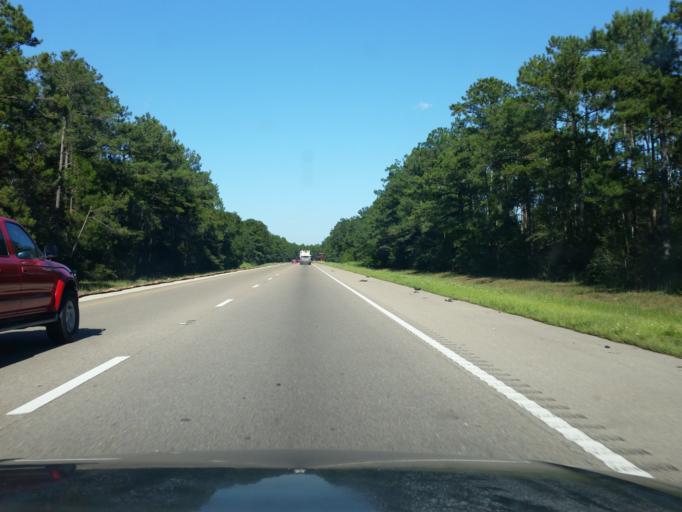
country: US
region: Mississippi
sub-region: Hancock County
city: Pearlington
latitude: 30.3299
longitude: -89.5507
